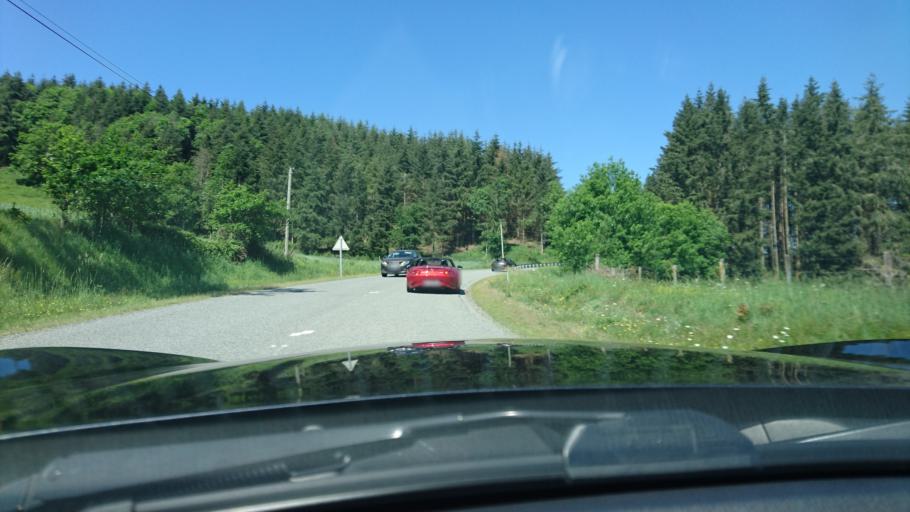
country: FR
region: Rhone-Alpes
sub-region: Departement de la Loire
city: Saint-Just-la-Pendue
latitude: 45.8809
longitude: 4.2845
